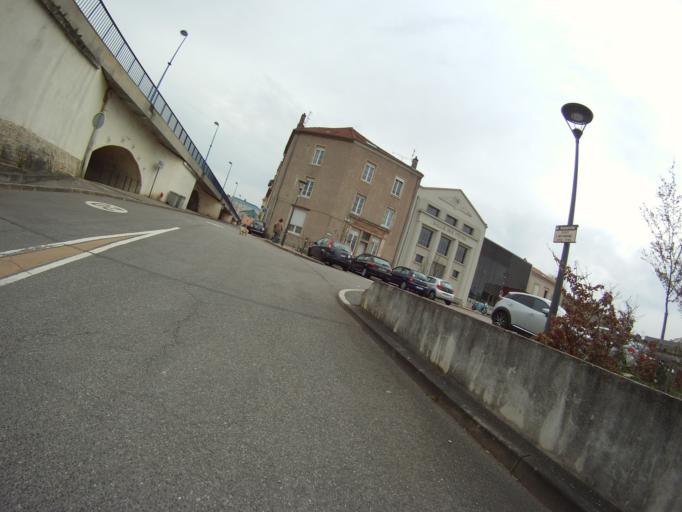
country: FR
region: Lorraine
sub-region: Departement de Meurthe-et-Moselle
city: Malzeville
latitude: 48.7060
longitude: 6.1845
